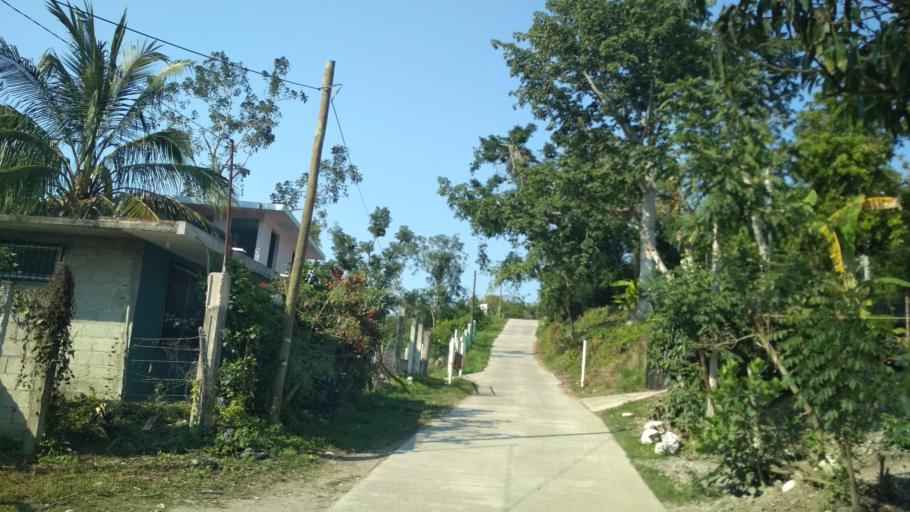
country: MX
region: Veracruz
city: Agua Dulce
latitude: 20.3930
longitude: -97.2107
